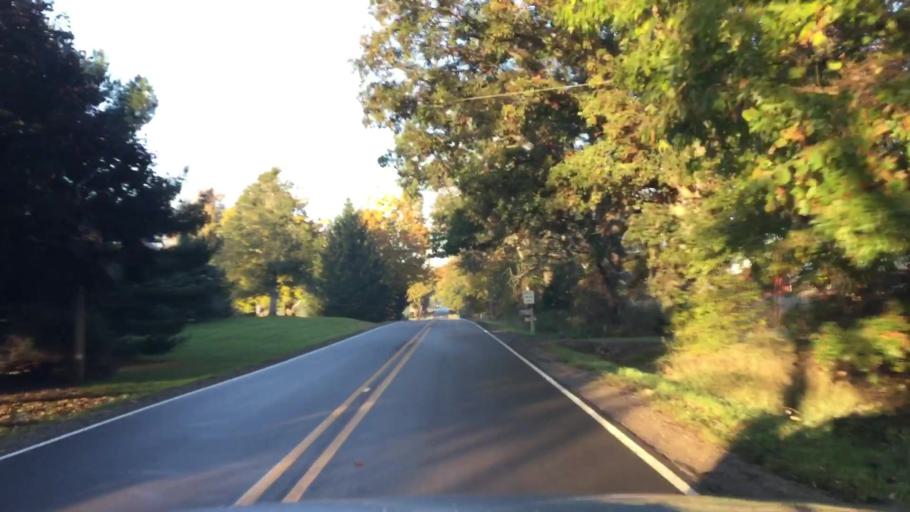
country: US
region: Michigan
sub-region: Genesee County
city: Argentine
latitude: 42.7603
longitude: -83.9266
